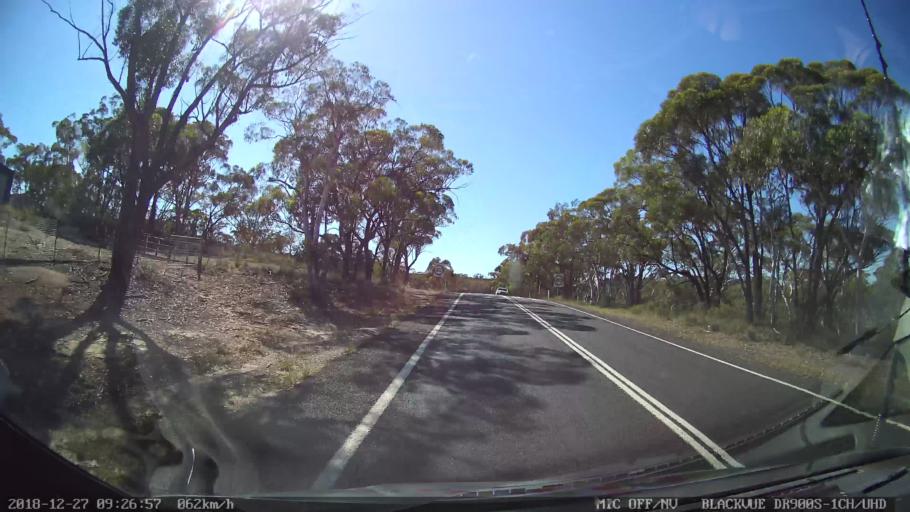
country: AU
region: New South Wales
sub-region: Lithgow
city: Portland
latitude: -33.1487
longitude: 149.9898
